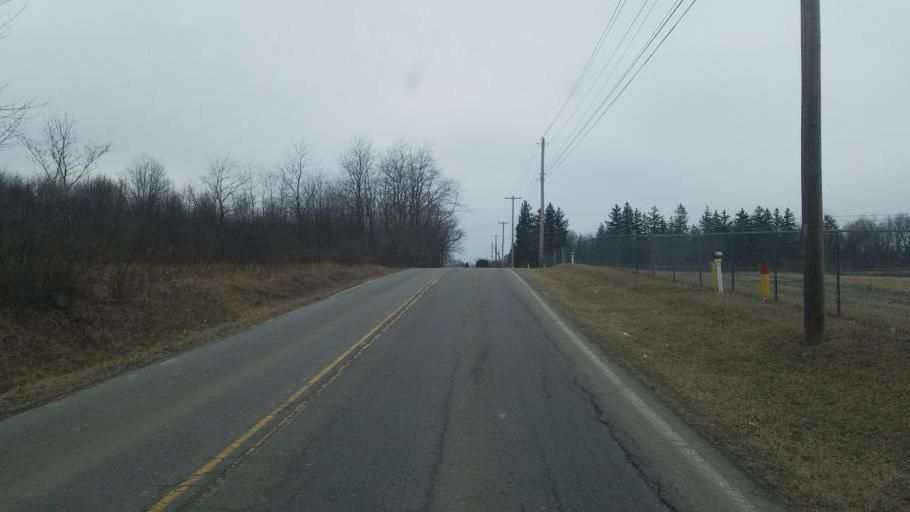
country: US
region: Ohio
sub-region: Richland County
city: Mansfield
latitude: 40.8060
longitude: -82.5351
